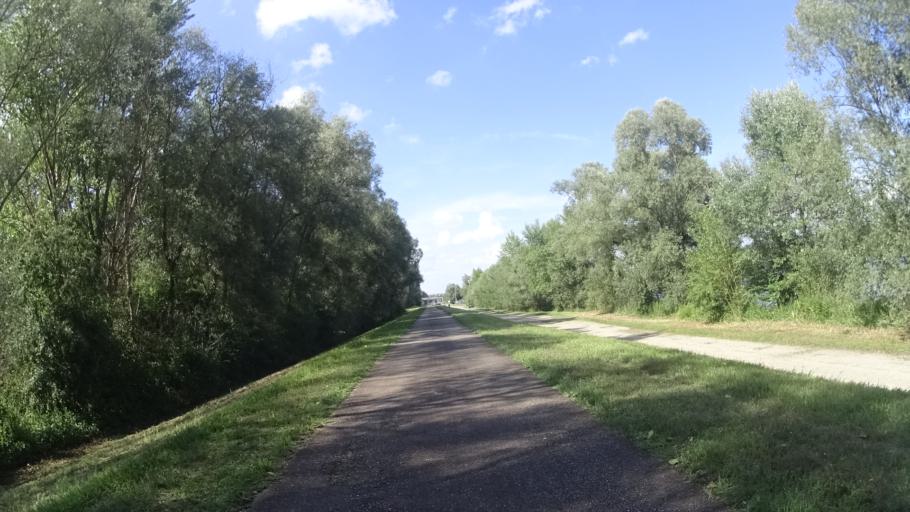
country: FR
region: Alsace
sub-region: Departement du Bas-Rhin
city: Seltz
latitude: 48.8531
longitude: 8.1074
